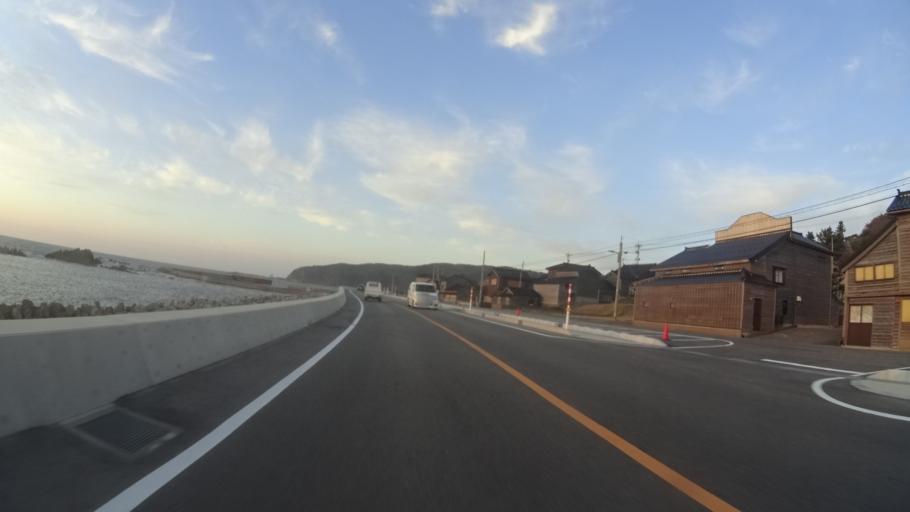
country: JP
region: Ishikawa
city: Nanao
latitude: 37.2798
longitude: 136.7339
